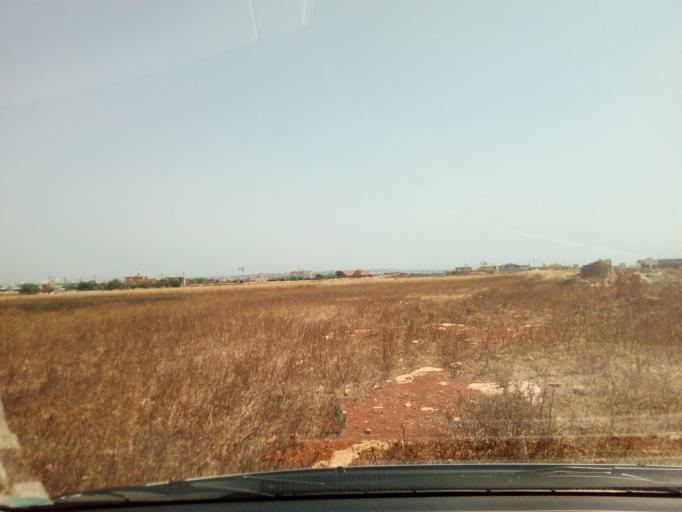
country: CY
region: Ammochostos
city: Liopetri
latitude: 34.9694
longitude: 33.8499
